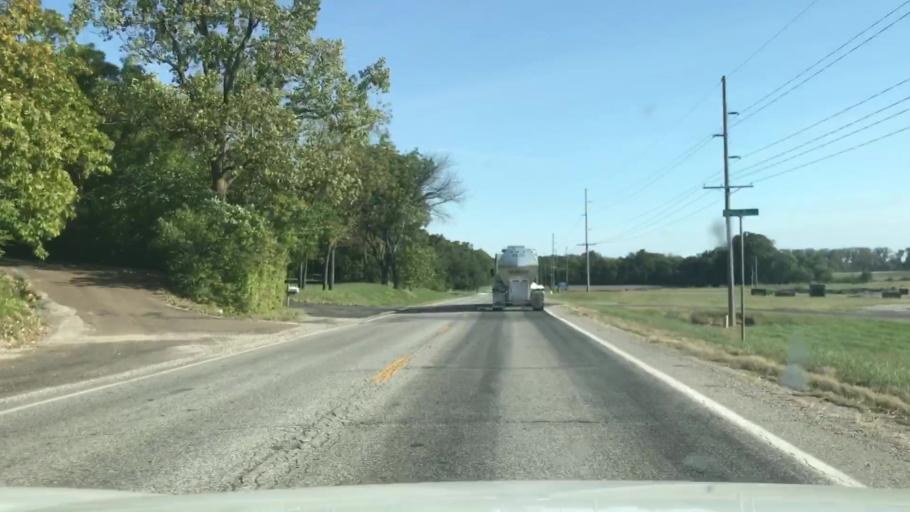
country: US
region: Illinois
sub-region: Adams County
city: Quincy
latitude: 39.8491
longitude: -91.3782
